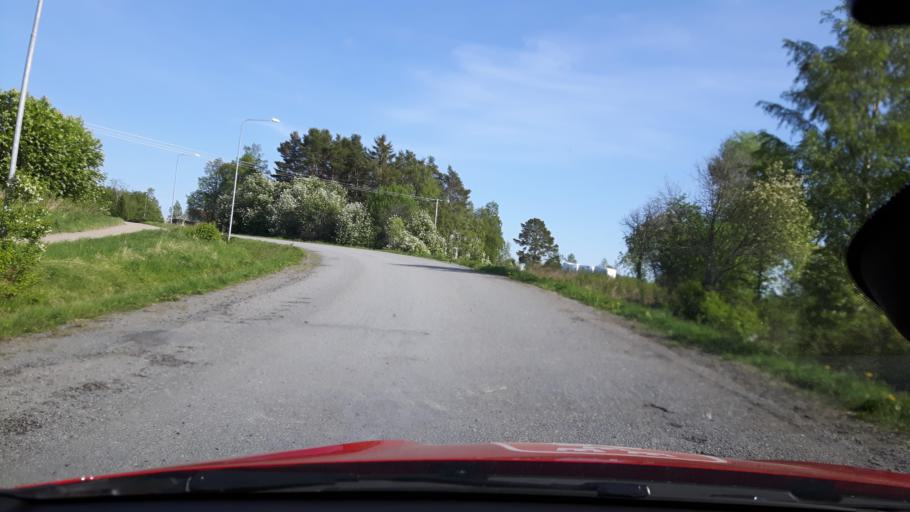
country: SE
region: Jaemtland
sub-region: Bergs Kommun
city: Hoverberg
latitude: 62.9221
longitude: 14.5083
